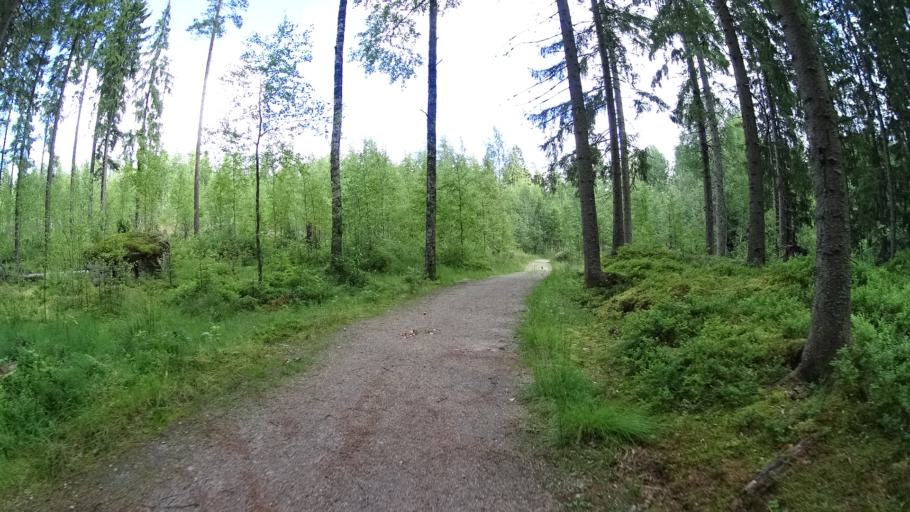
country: FI
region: Uusimaa
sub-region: Helsinki
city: Kauniainen
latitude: 60.3200
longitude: 24.6821
